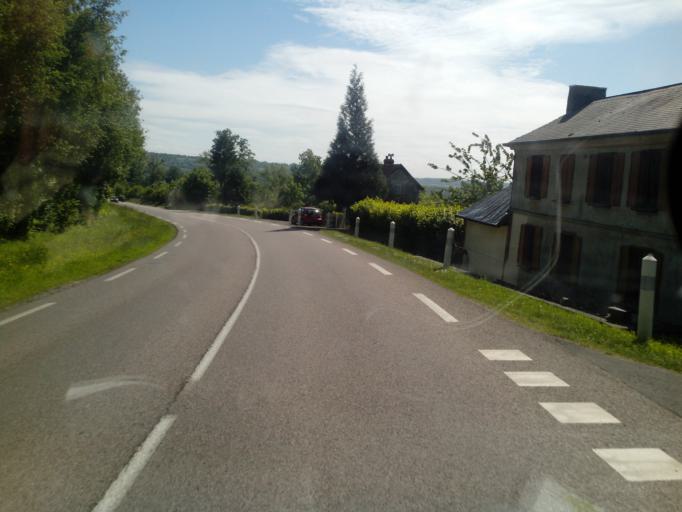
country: FR
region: Lower Normandy
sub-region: Departement du Calvados
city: Ablon
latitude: 49.3155
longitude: 0.2618
